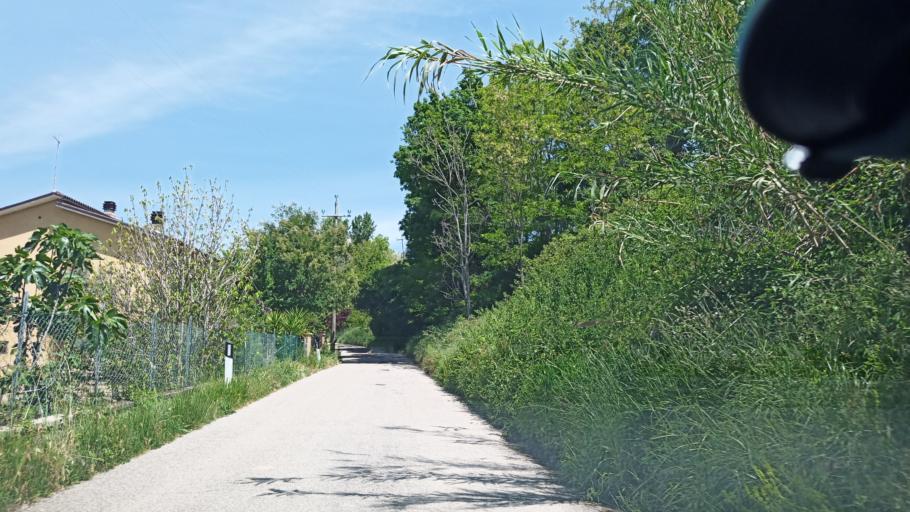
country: IT
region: Latium
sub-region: Provincia di Rieti
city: Torri in Sabina
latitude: 42.3569
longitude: 12.6346
